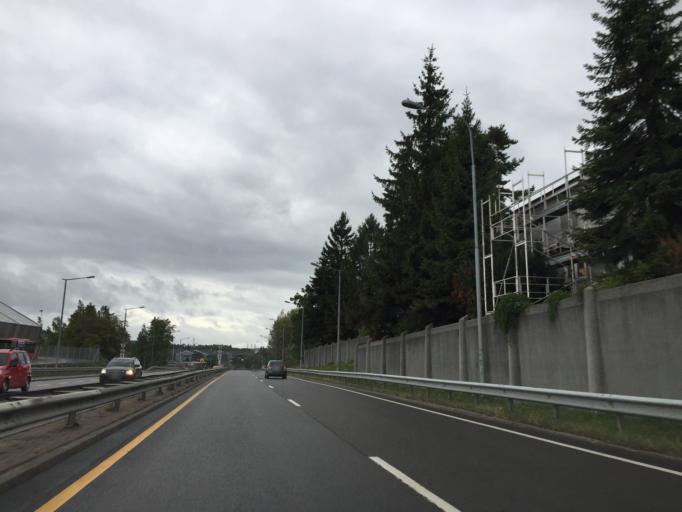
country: NO
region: Akershus
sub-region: Lorenskog
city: Kjenn
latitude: 59.9525
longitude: 10.8883
